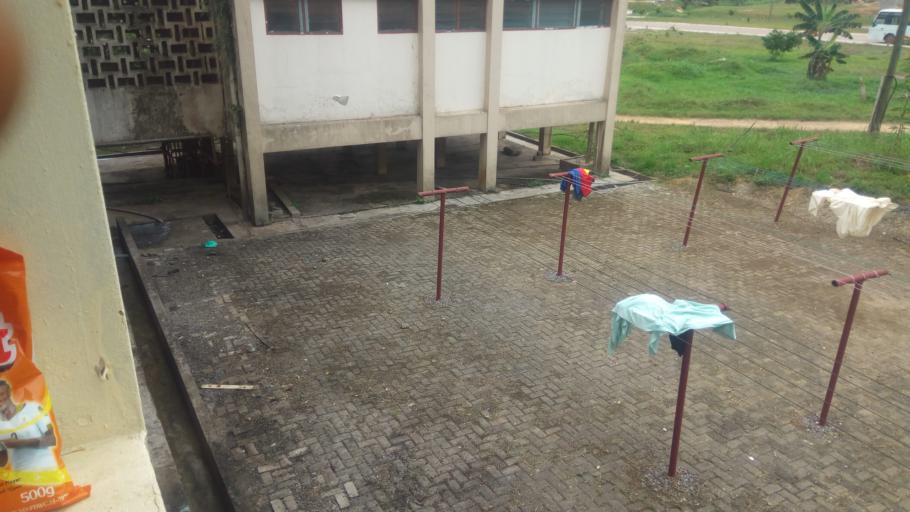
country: GH
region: Western
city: Tarkwa
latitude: 5.2979
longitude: -2.0037
